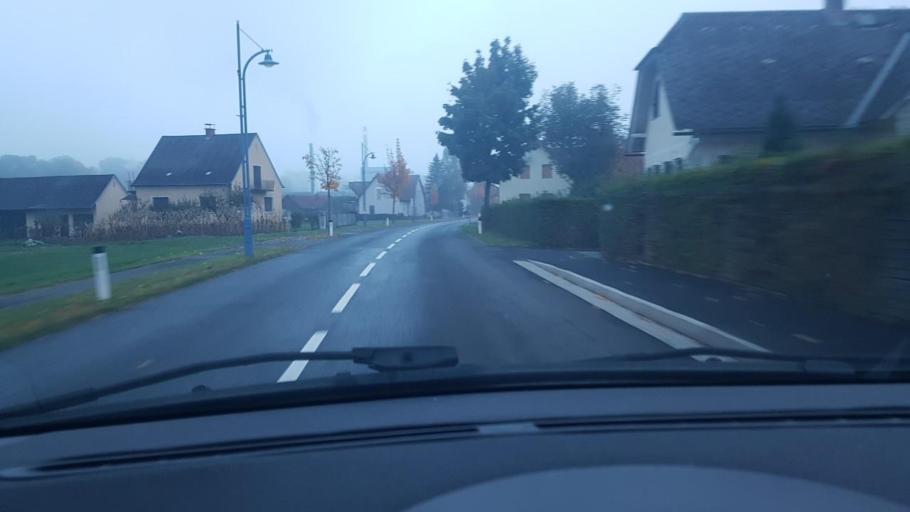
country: AT
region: Styria
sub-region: Politischer Bezirk Leibnitz
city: Obervogau
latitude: 46.7490
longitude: 15.5826
